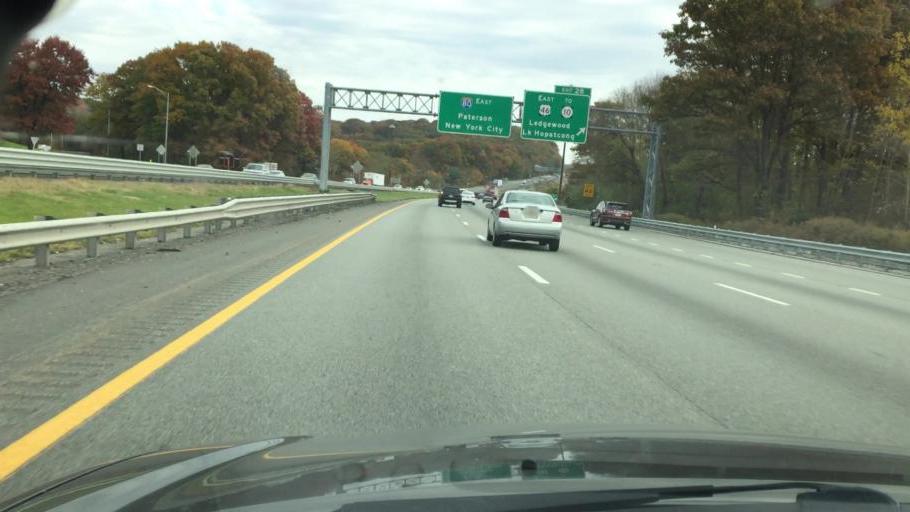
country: US
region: New Jersey
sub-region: Morris County
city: Netcong
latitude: 40.8923
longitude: -74.6711
